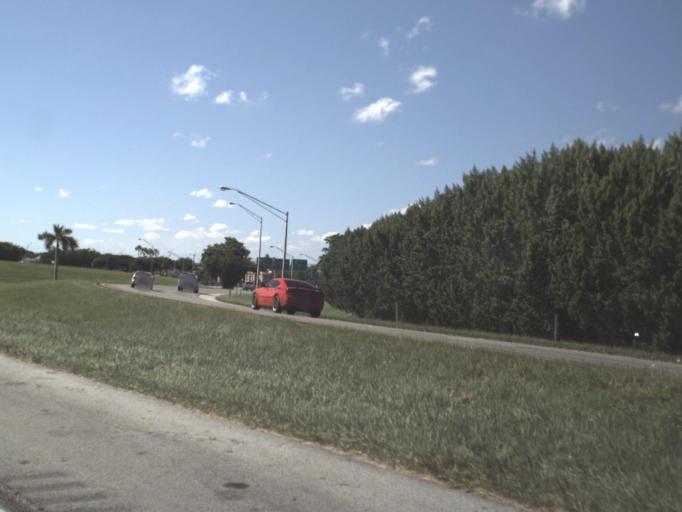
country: US
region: Florida
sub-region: Miami-Dade County
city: The Crossings
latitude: 25.6897
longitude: -80.3894
